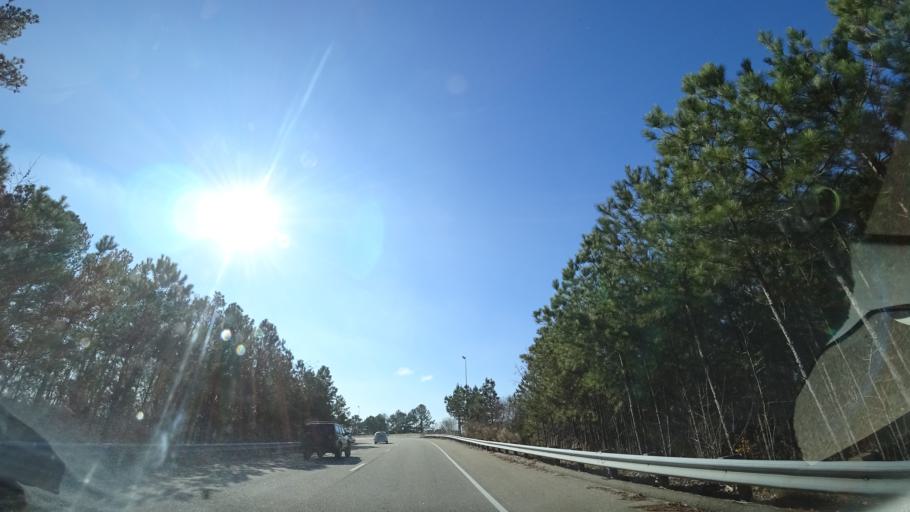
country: US
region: Virginia
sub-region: City of Hampton
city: Hampton
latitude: 37.0533
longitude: -76.4061
